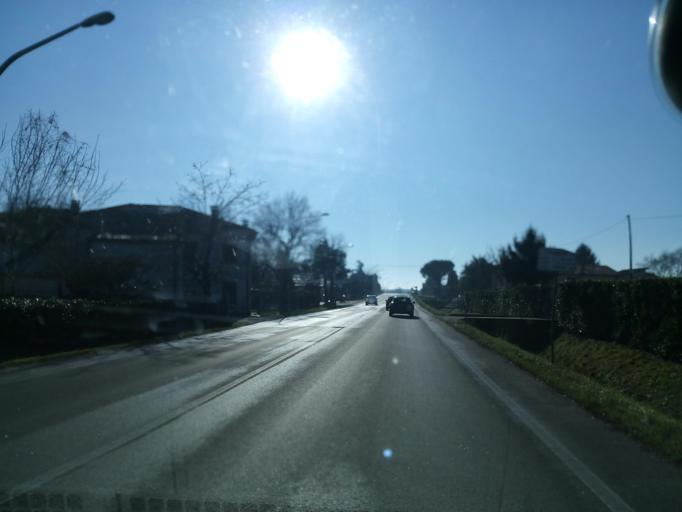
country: IT
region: Veneto
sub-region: Provincia di Venezia
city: Stigliano
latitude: 45.5285
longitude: 12.0508
